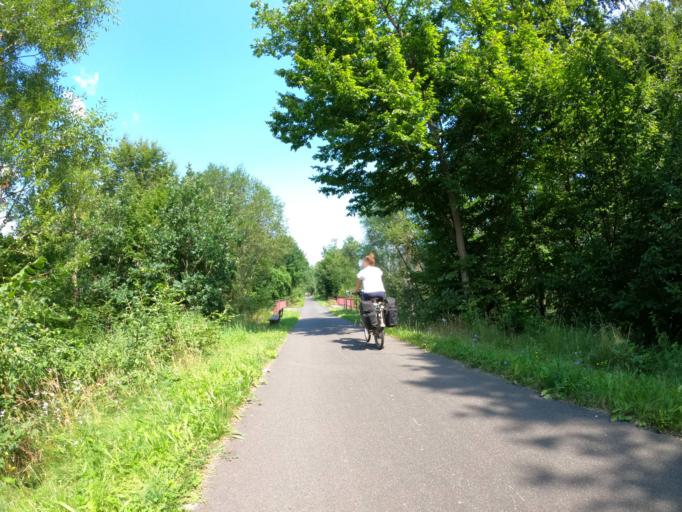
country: DE
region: Brandenburg
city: Templin
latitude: 53.2433
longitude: 13.5048
